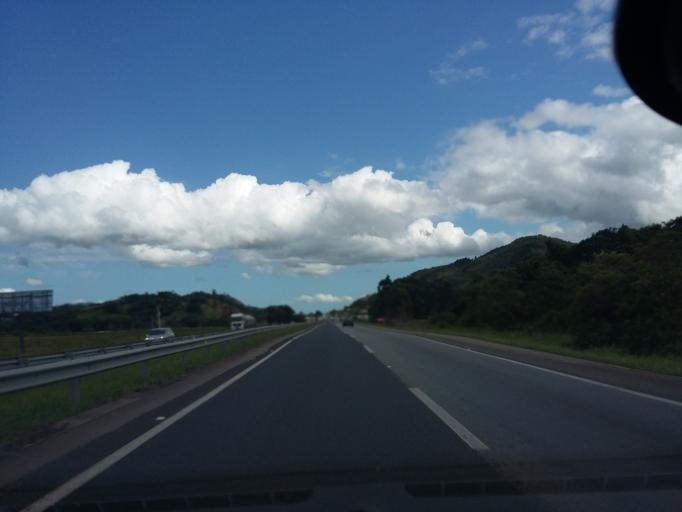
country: BR
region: Santa Catarina
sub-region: Tijucas
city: Tijucas
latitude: -27.2714
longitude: -48.6317
